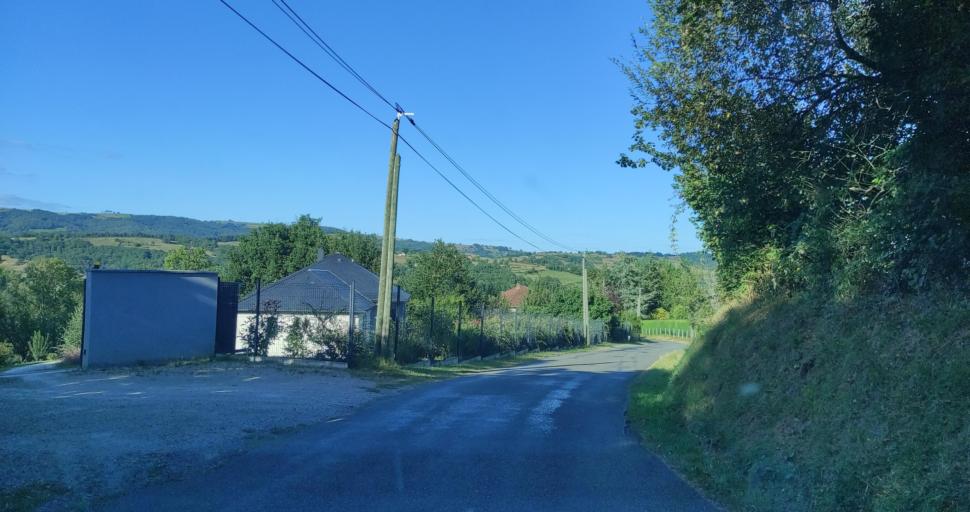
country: FR
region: Midi-Pyrenees
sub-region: Departement de l'Aveyron
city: Firmi
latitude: 44.5296
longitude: 2.3170
